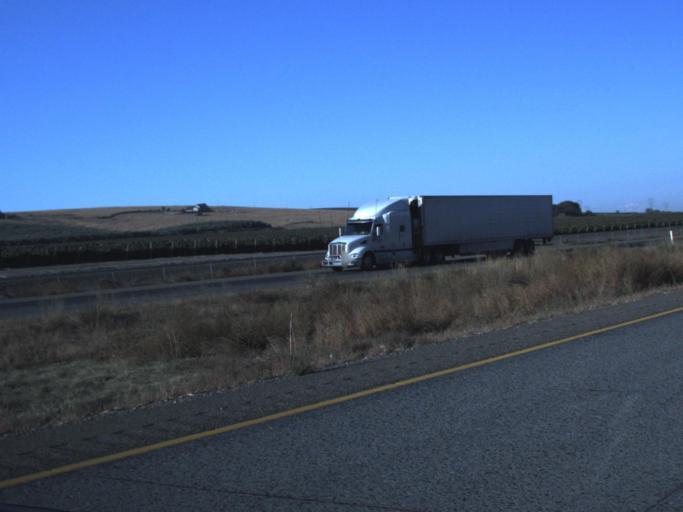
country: US
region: Washington
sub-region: Yakima County
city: Granger
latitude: 46.3310
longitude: -120.1168
